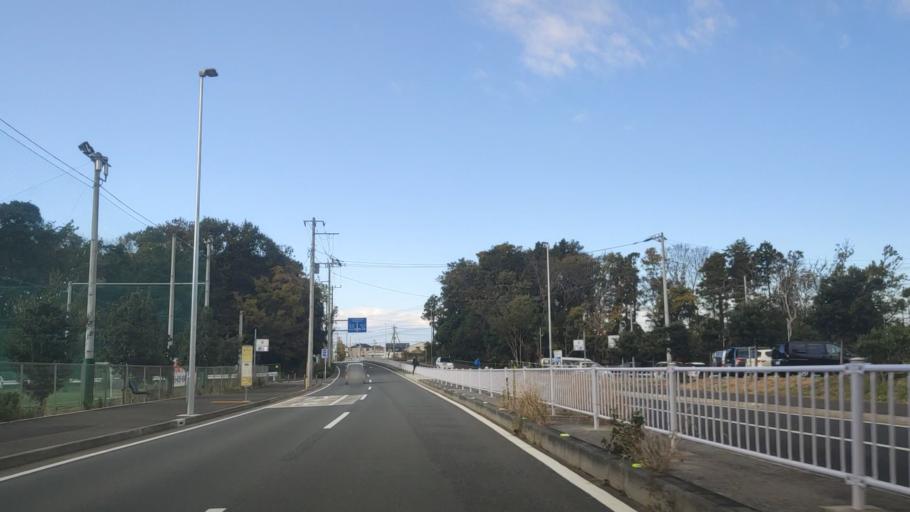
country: JP
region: Kanagawa
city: Minami-rinkan
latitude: 35.4265
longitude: 139.4873
